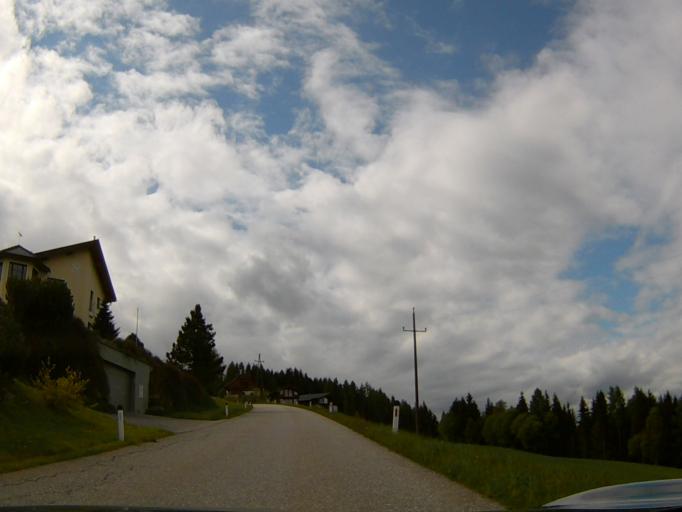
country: AT
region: Carinthia
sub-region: Politischer Bezirk Villach Land
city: Stockenboi
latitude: 46.7372
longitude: 13.5573
